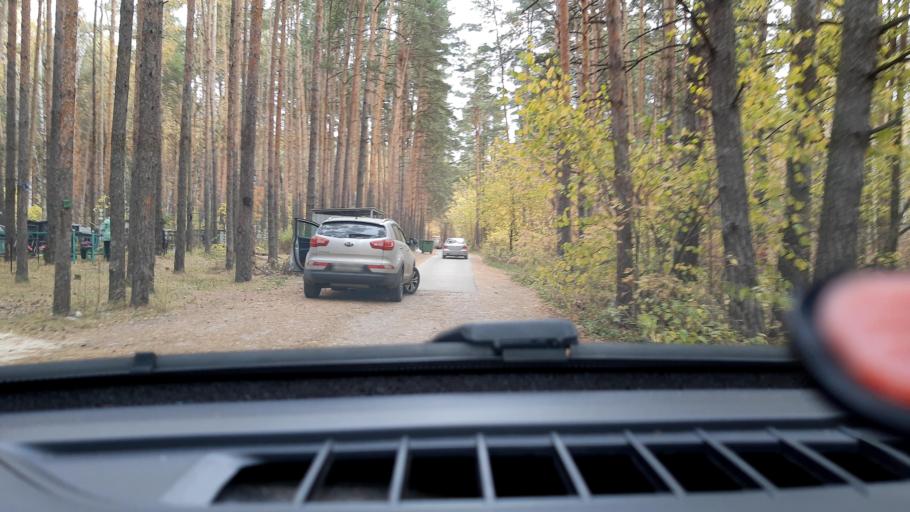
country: RU
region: Nizjnij Novgorod
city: Gorbatovka
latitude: 56.2874
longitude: 43.8233
